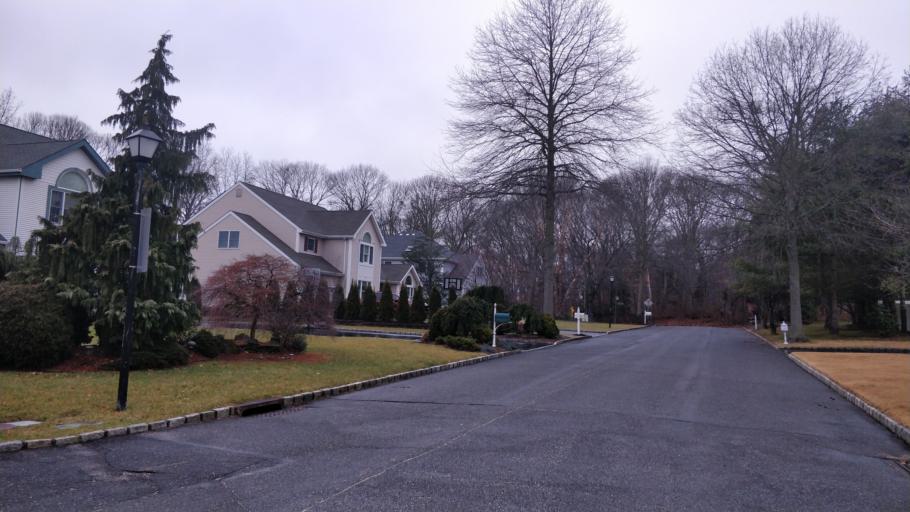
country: US
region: New York
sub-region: Suffolk County
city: Hauppauge
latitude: 40.8286
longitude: -73.2046
